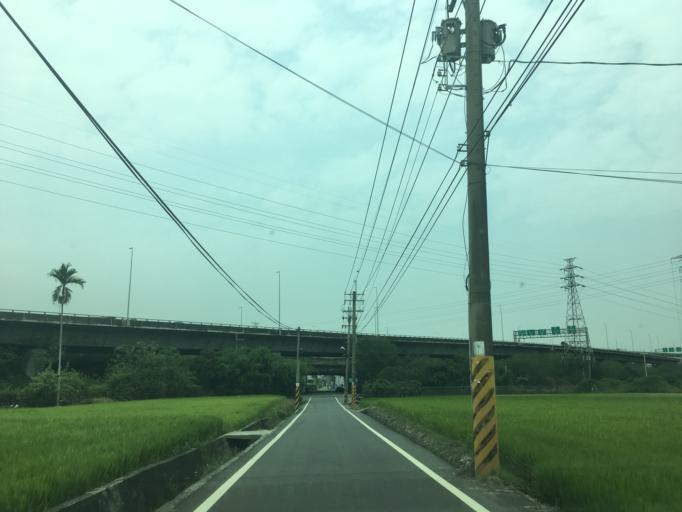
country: TW
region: Taiwan
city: Zhongxing New Village
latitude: 24.0446
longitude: 120.6795
